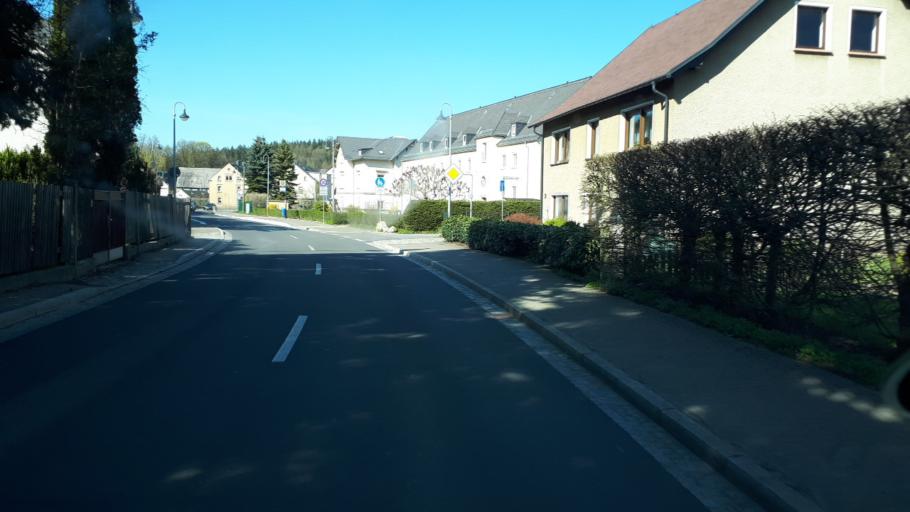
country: DE
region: Saxony
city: Gelenau
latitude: 50.7769
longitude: 12.9708
